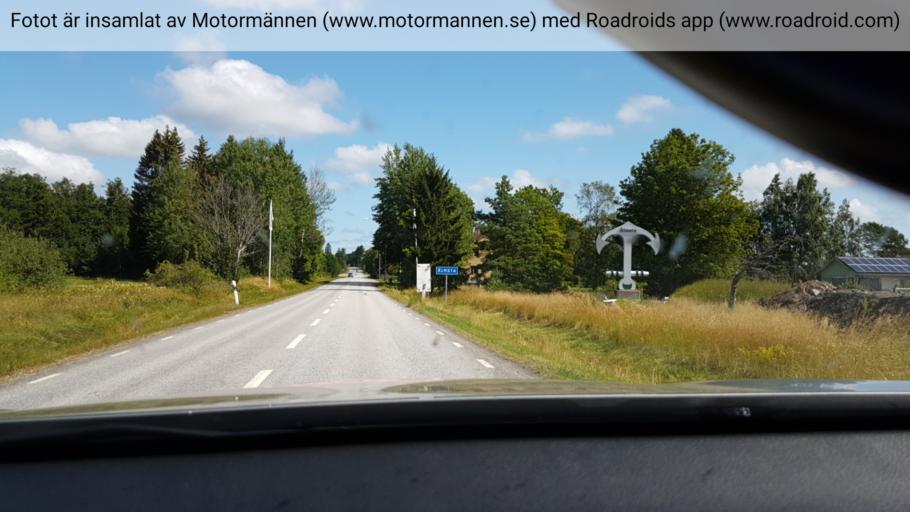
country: SE
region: Stockholm
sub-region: Norrtalje Kommun
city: Hallstavik
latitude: 59.9583
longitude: 18.7939
